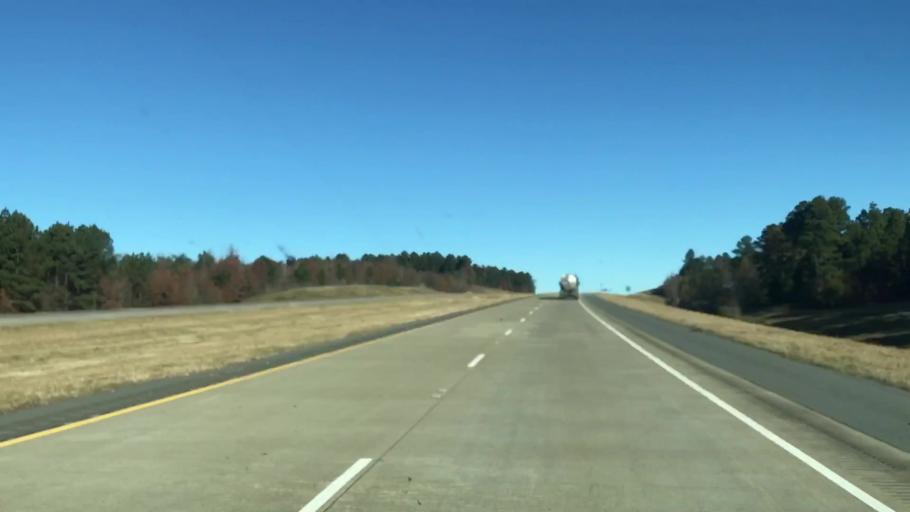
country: US
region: Louisiana
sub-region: Caddo Parish
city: Vivian
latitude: 32.9854
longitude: -93.9105
